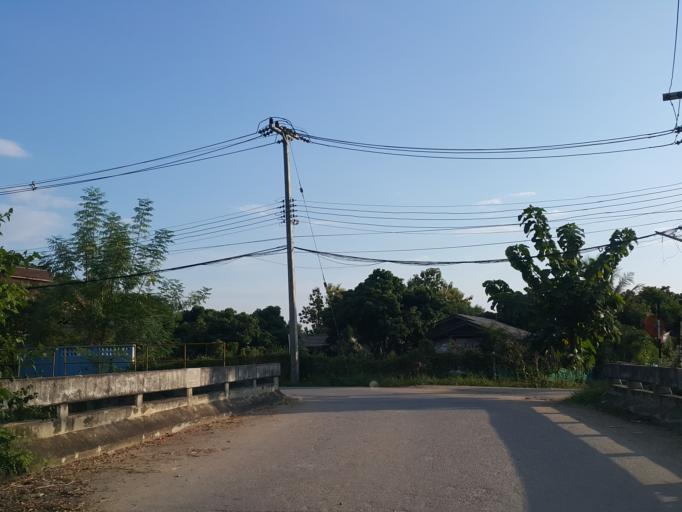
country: TH
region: Chiang Mai
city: San Kamphaeng
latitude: 18.7477
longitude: 99.0932
